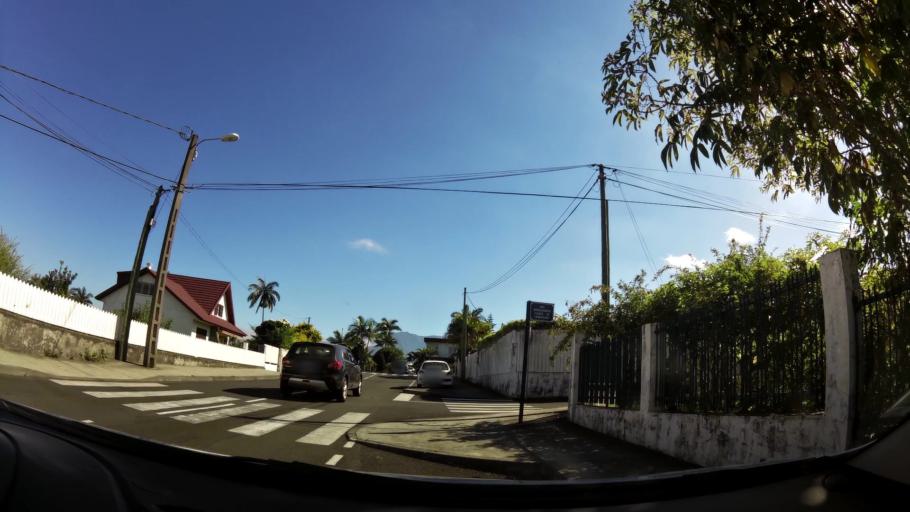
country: RE
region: Reunion
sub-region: Reunion
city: Le Tampon
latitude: -21.2736
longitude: 55.5146
